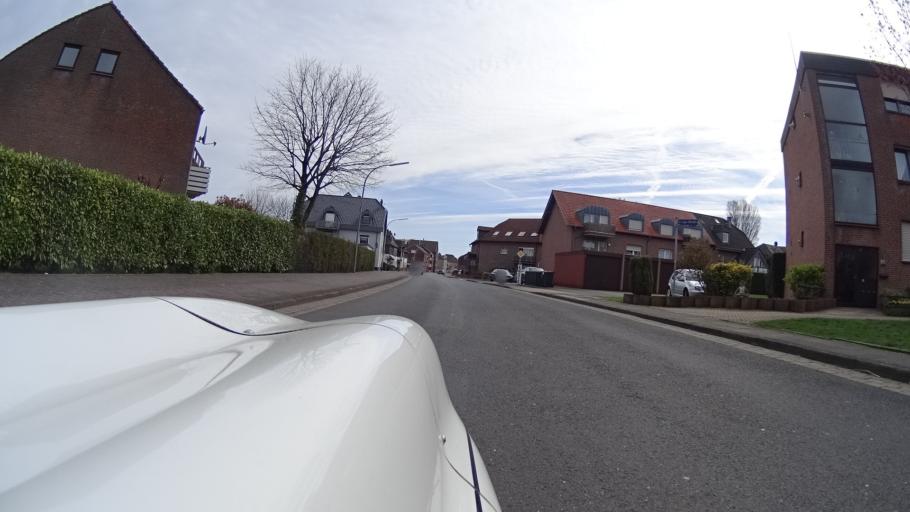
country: DE
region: North Rhine-Westphalia
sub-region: Regierungsbezirk Dusseldorf
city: Goch
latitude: 51.6792
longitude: 6.1481
